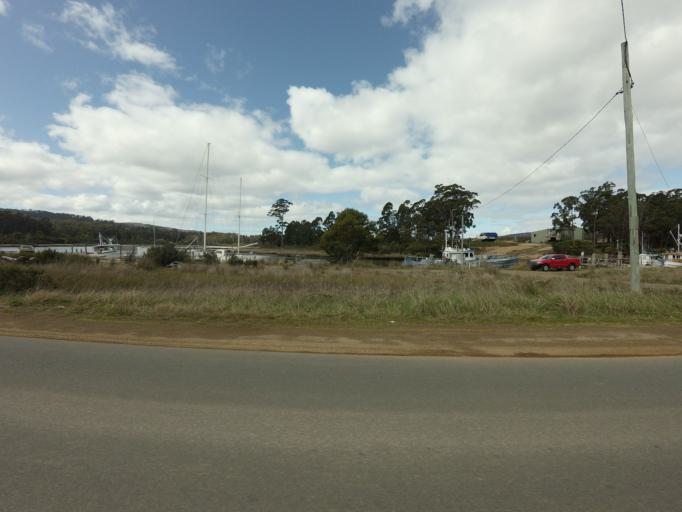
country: AU
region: Tasmania
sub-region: Huon Valley
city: Geeveston
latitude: -43.3284
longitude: 146.9708
